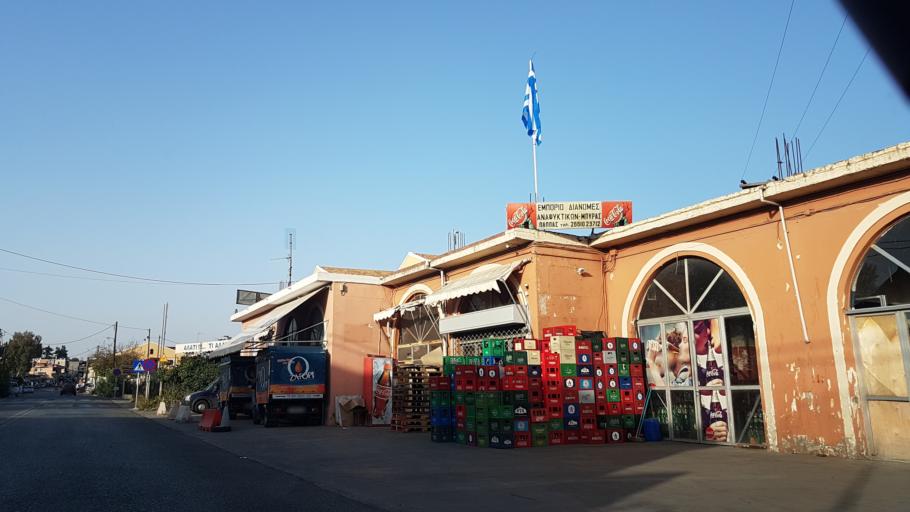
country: GR
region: Ionian Islands
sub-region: Nomos Kerkyras
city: Kanali
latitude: 39.5974
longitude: 19.8933
